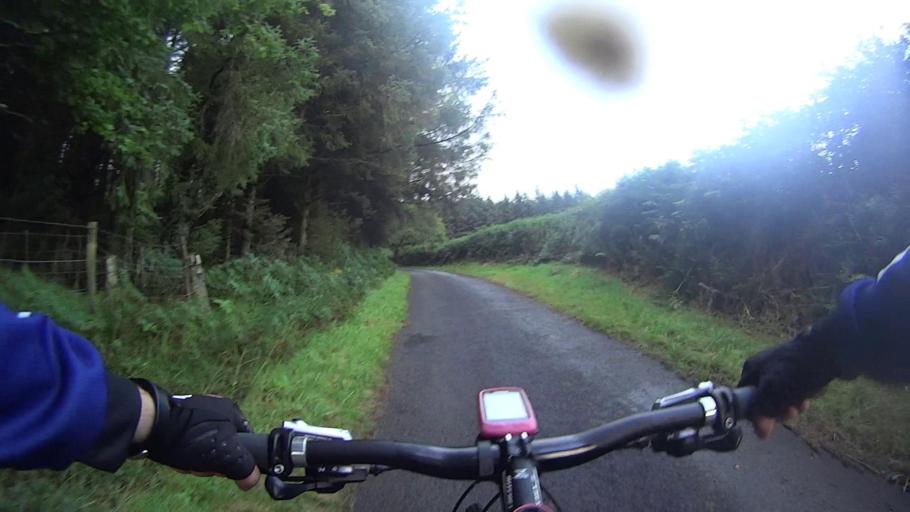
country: GB
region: Wales
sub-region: County of Ceredigion
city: Bow Street
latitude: 52.4215
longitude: -3.9166
